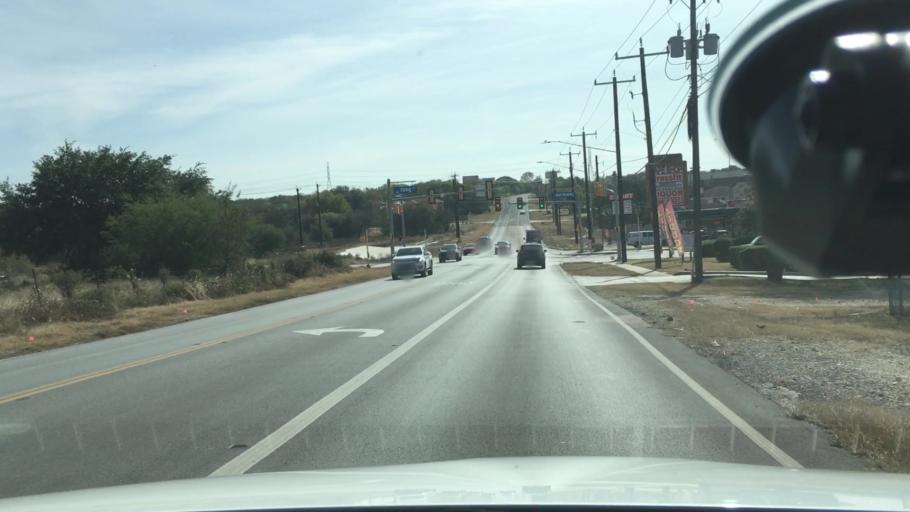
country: US
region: Texas
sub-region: Bexar County
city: Hollywood Park
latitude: 29.5799
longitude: -98.4207
